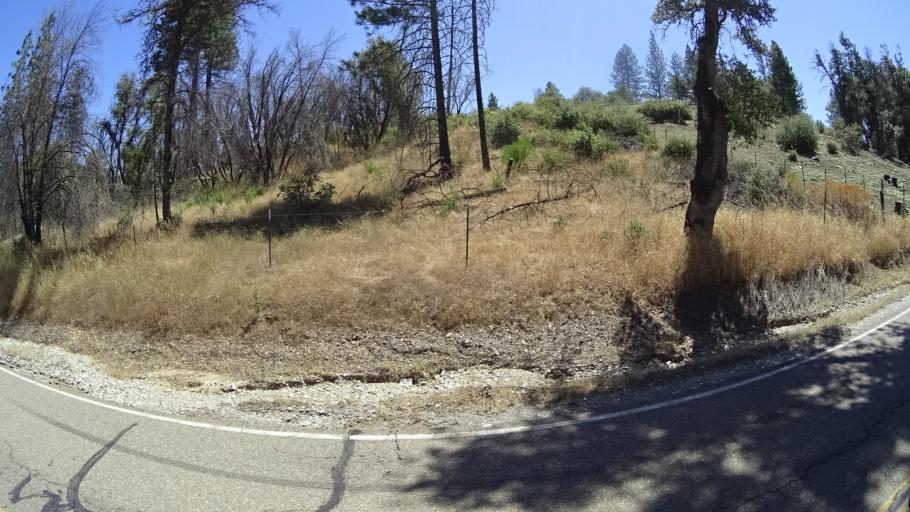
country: US
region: California
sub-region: Calaveras County
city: Mountain Ranch
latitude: 38.2508
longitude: -120.5205
